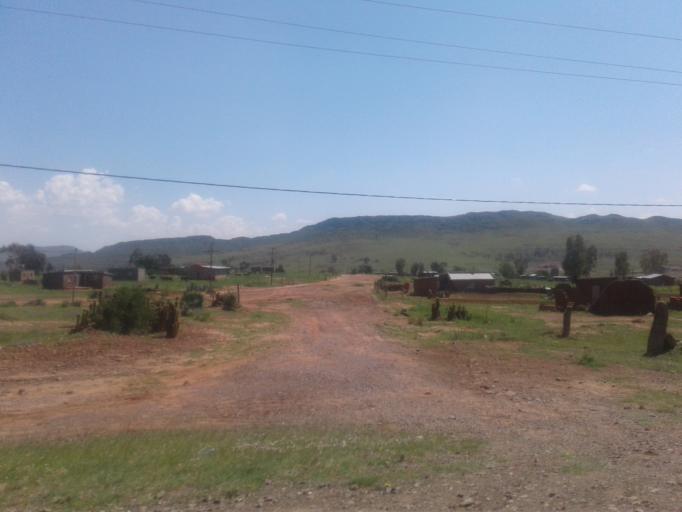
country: LS
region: Mafeteng
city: Mafeteng
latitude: -29.7546
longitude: 27.1306
